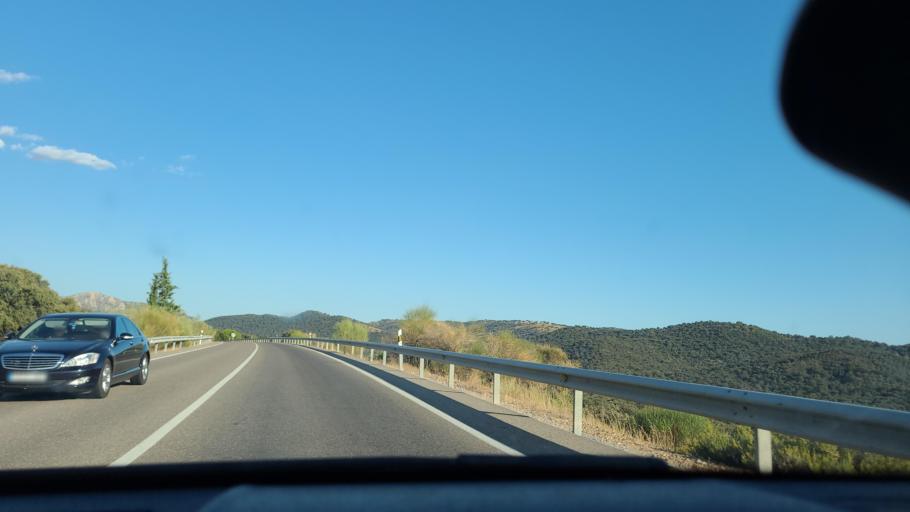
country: ES
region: Andalusia
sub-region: Province of Cordoba
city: Espiel
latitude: 38.1923
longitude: -5.0959
